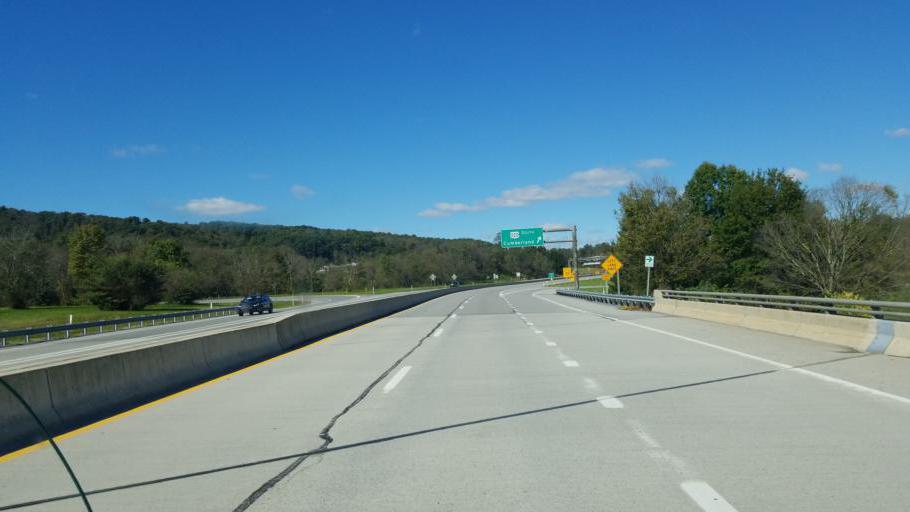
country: US
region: Pennsylvania
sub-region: Bedford County
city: Bedford
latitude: 40.0262
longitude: -78.5137
